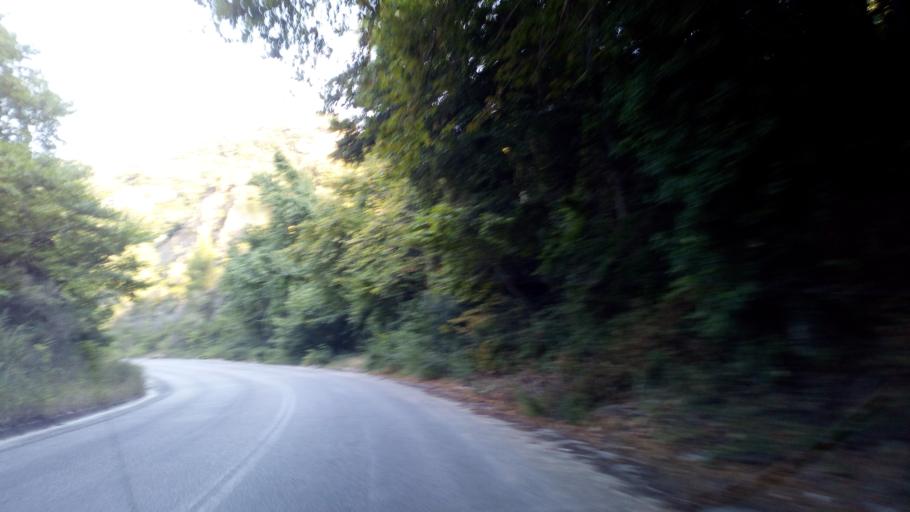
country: GR
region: Central Macedonia
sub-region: Nomos Chalkidikis
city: Neos Marmaras
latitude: 40.1705
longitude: 23.8507
